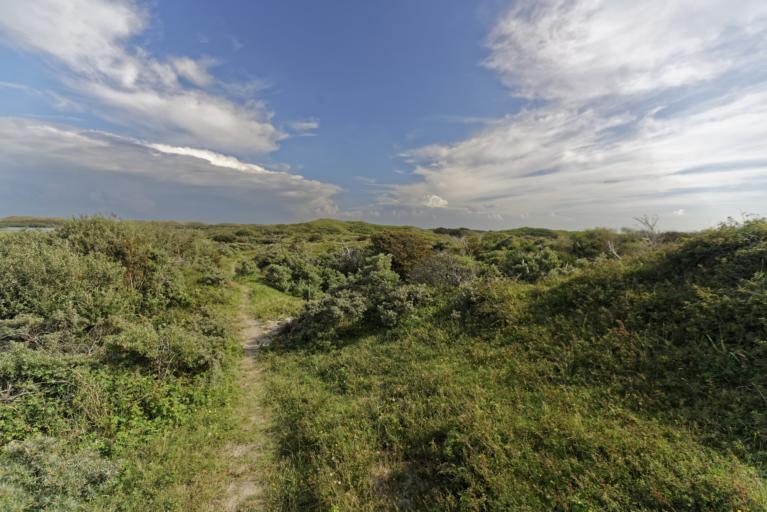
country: NL
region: North Holland
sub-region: Gemeente Texel
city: Den Burg
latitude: 53.1194
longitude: 4.7864
